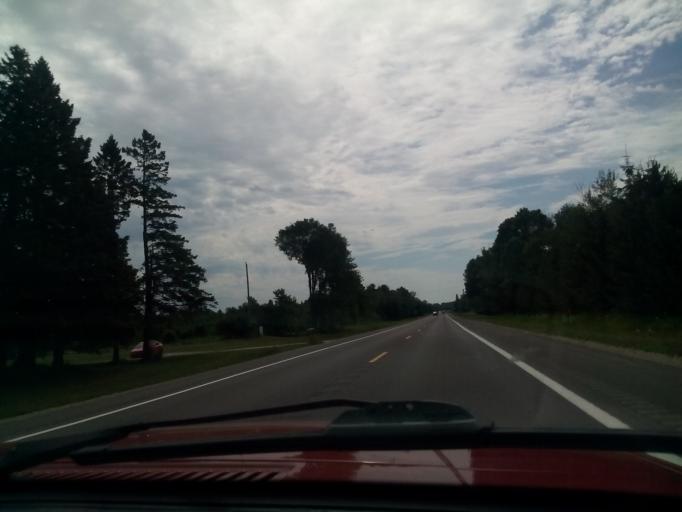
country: US
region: Michigan
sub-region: Schoolcraft County
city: Manistique
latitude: 46.0742
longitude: -85.9583
